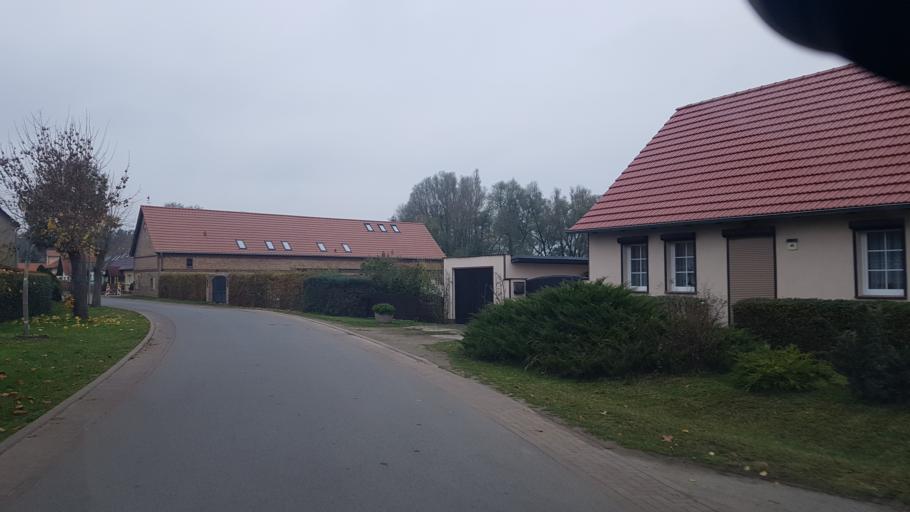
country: DE
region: Brandenburg
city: Sonnenberg
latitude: 52.9357
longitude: 13.0706
